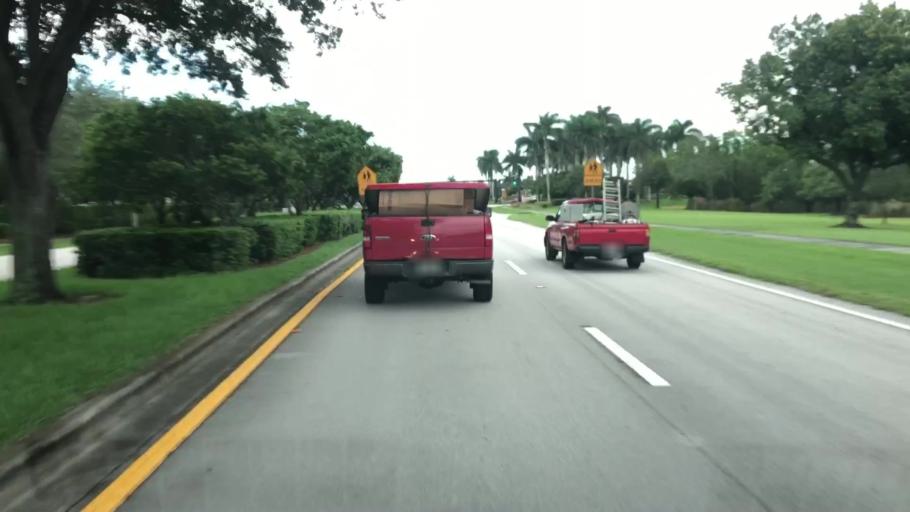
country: US
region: Florida
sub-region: Broward County
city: Coral Springs
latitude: 26.3106
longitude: -80.2789
